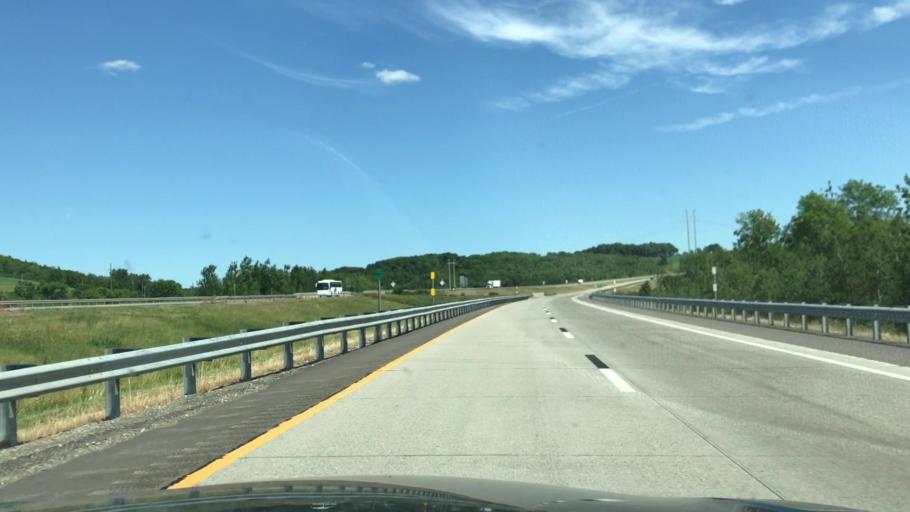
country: US
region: New York
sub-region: Steuben County
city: Wayland
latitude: 42.5403
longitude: -77.5714
